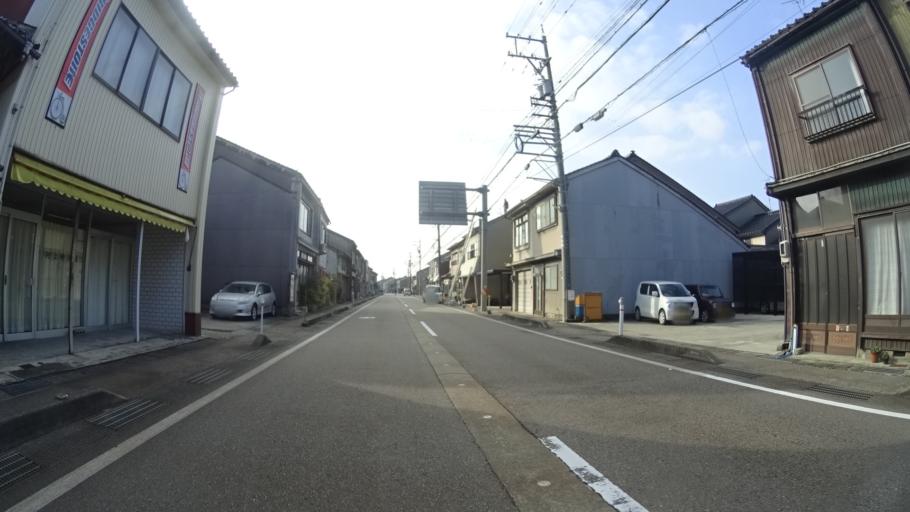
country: JP
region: Toyama
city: Himi
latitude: 36.8715
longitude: 136.9830
